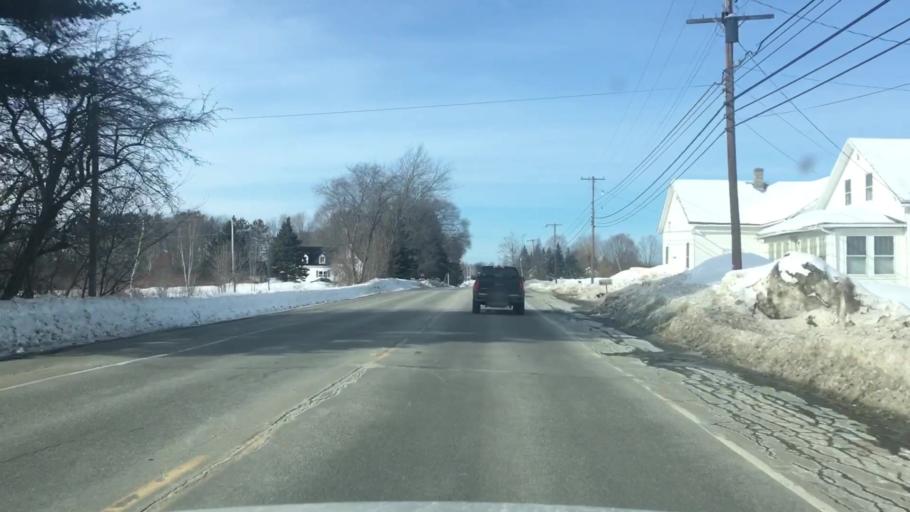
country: US
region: Maine
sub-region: Penobscot County
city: Charleston
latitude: 45.0125
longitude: -69.0267
